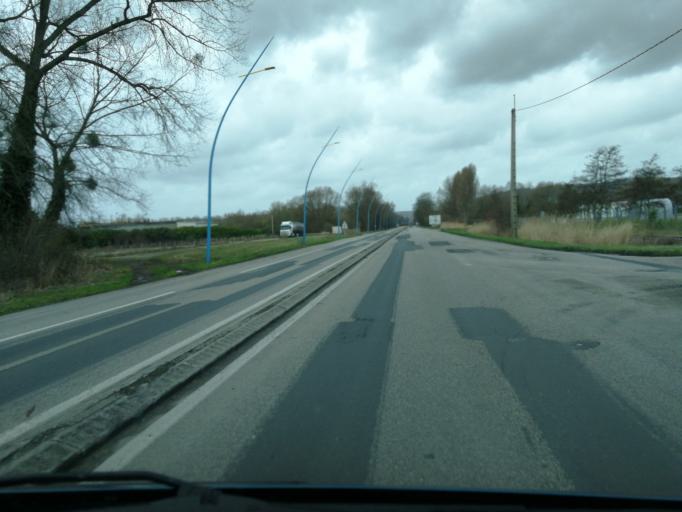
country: FR
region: Haute-Normandie
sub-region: Departement de l'Eure
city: Quillebeuf-sur-Seine
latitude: 49.4806
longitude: 0.5328
